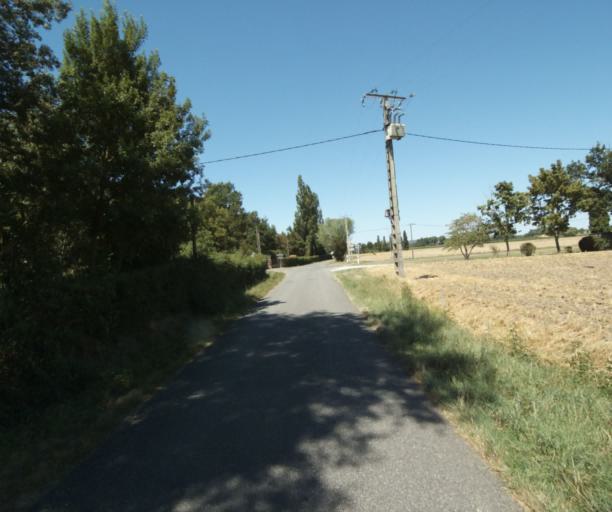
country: FR
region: Midi-Pyrenees
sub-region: Departement de la Haute-Garonne
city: Revel
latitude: 43.4566
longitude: 1.9485
